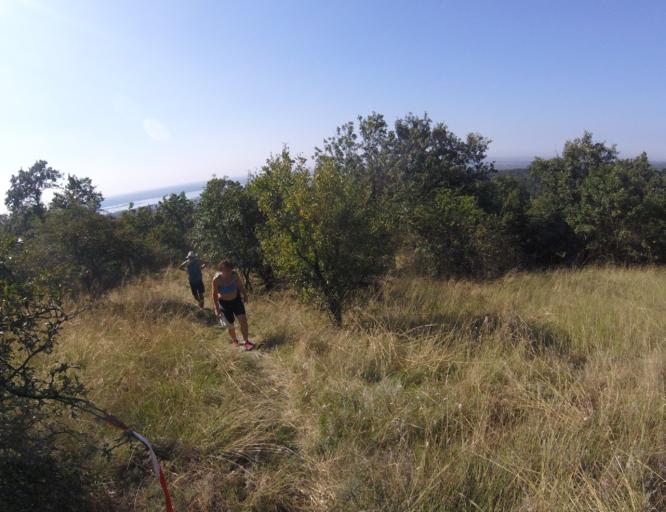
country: HU
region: Fejer
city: Lovasbereny
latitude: 47.2590
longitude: 18.5902
